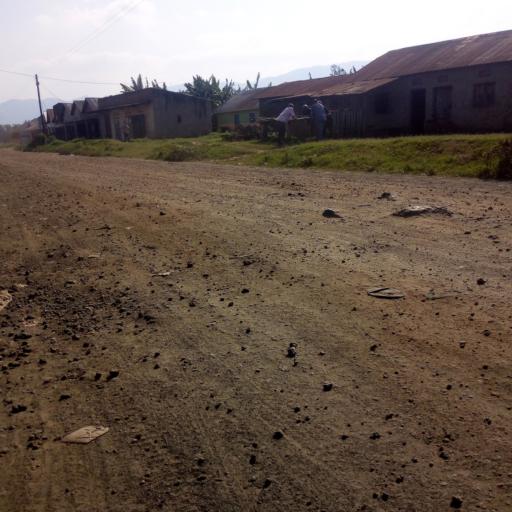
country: UG
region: Western Region
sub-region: Kisoro District
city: Kisoro
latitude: -1.2447
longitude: 29.7136
